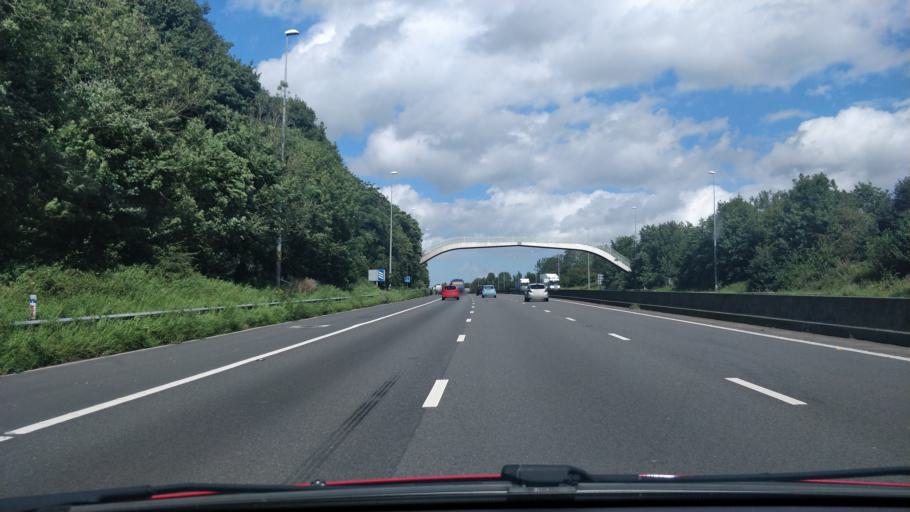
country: GB
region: England
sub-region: Borough of Wigan
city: Shevington
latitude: 53.5811
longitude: -2.6948
